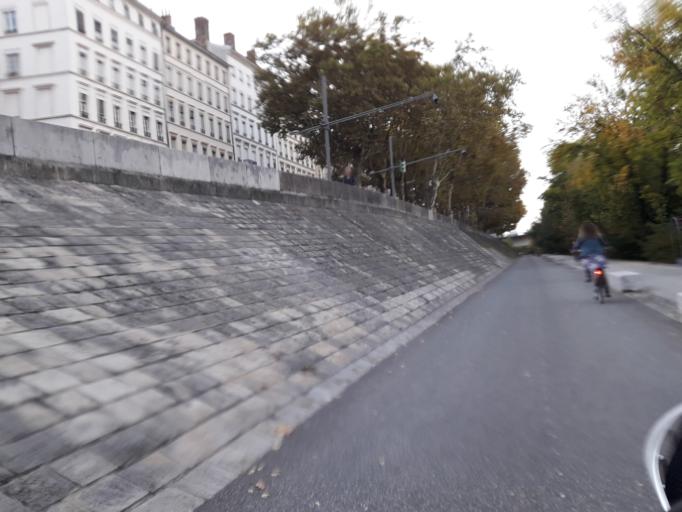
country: FR
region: Rhone-Alpes
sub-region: Departement du Rhone
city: Caluire-et-Cuire
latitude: 45.7717
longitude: 4.8407
